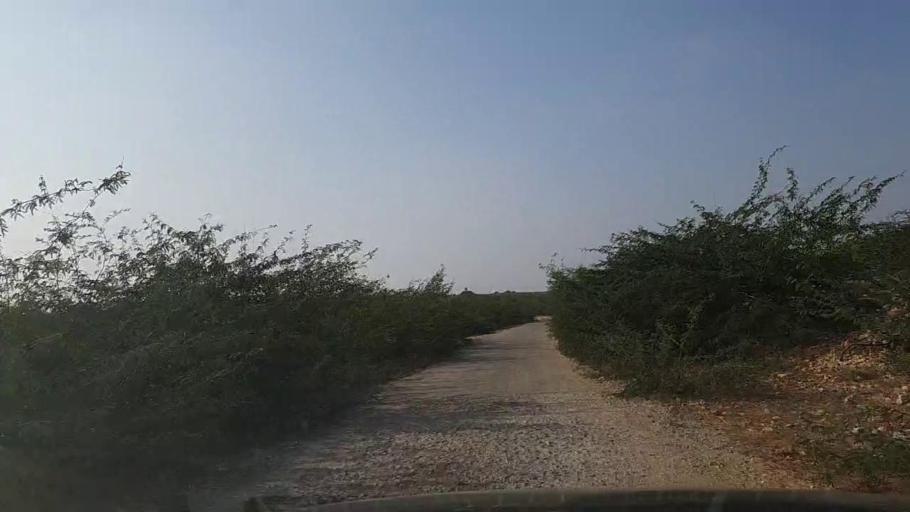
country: PK
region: Sindh
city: Gharo
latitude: 24.7549
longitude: 67.5307
